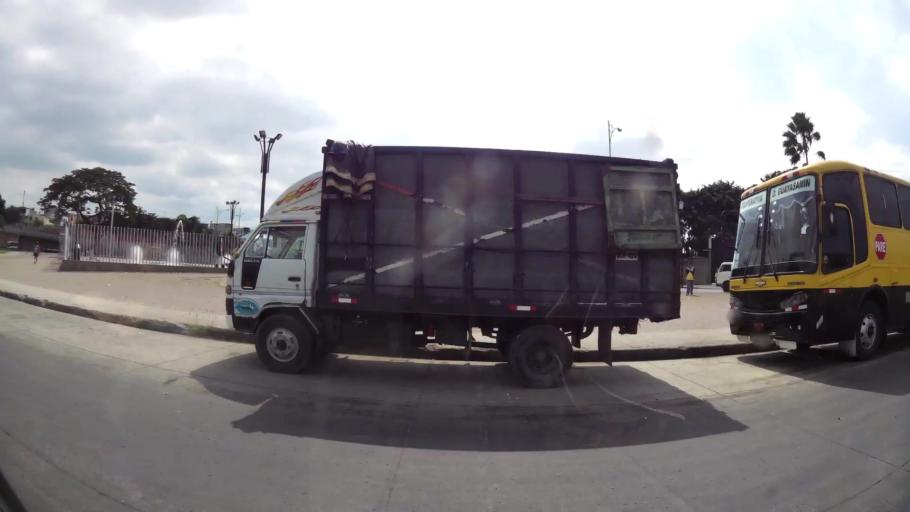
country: EC
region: Guayas
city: Santa Lucia
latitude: -2.0904
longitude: -79.9359
